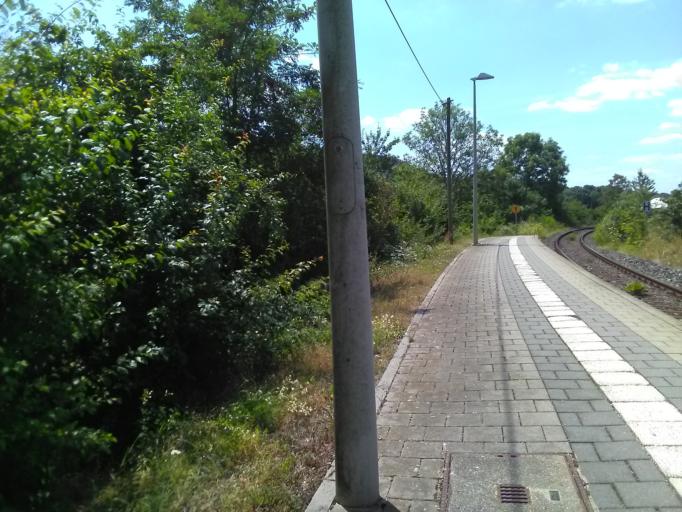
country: DE
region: Bavaria
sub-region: Upper Franconia
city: Weissenohe
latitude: 49.6287
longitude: 11.2490
